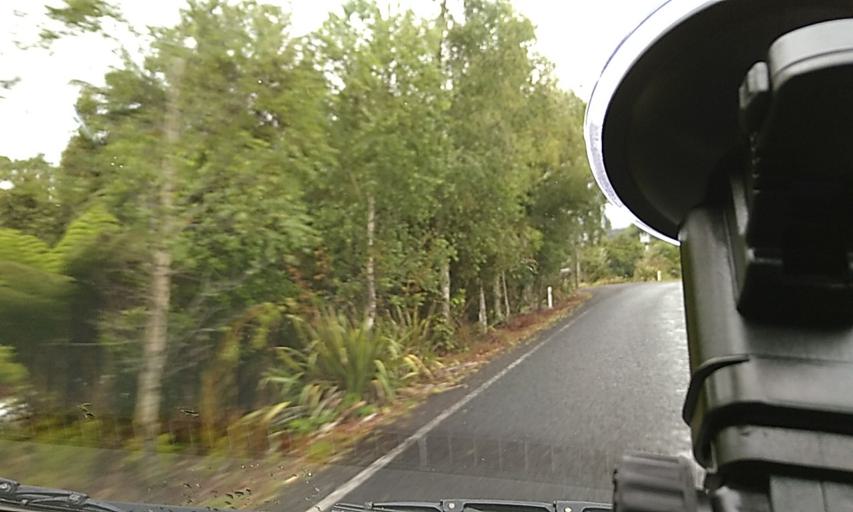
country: NZ
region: Auckland
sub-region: Auckland
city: Pukekohe East
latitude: -37.3198
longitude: 174.9300
